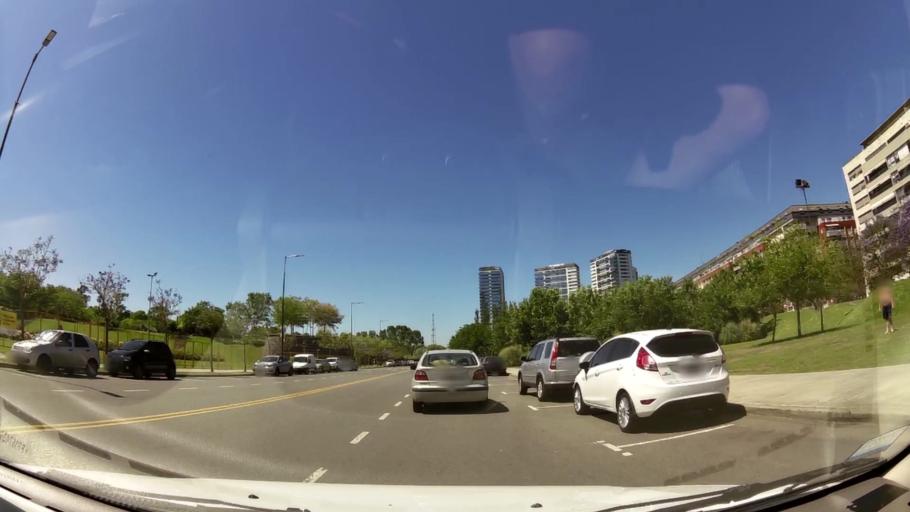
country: AR
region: Buenos Aires F.D.
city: Buenos Aires
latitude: -34.6153
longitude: -58.3606
